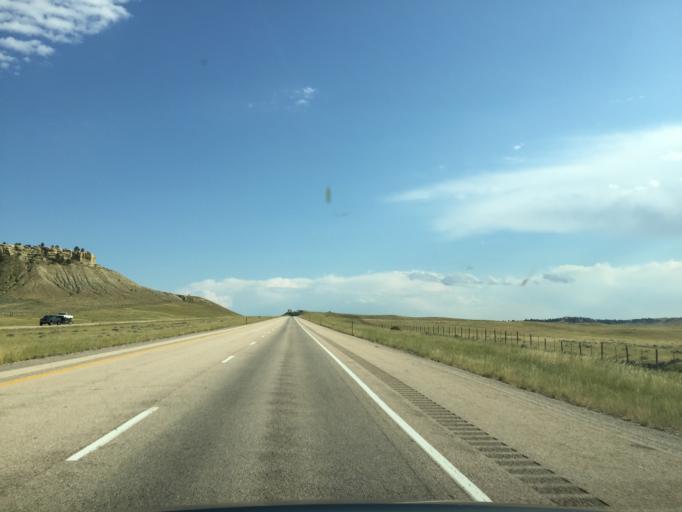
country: US
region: Wyoming
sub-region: Natrona County
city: Bar Nunn
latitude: 43.2657
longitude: -106.3906
